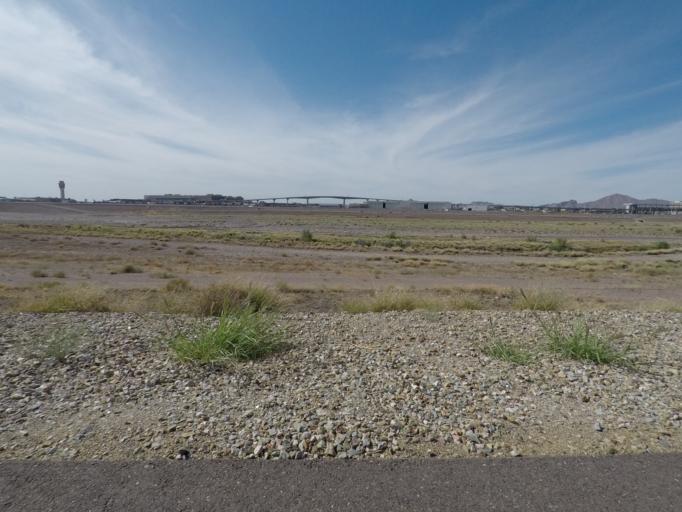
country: US
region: Arizona
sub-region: Maricopa County
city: Tempe Junction
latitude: 33.4277
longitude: -111.9880
